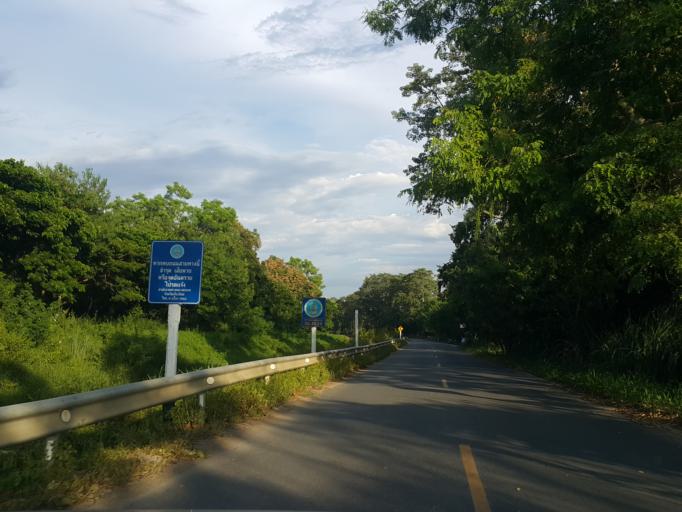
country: TH
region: Chiang Mai
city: San Sai
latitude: 18.9187
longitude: 99.0025
